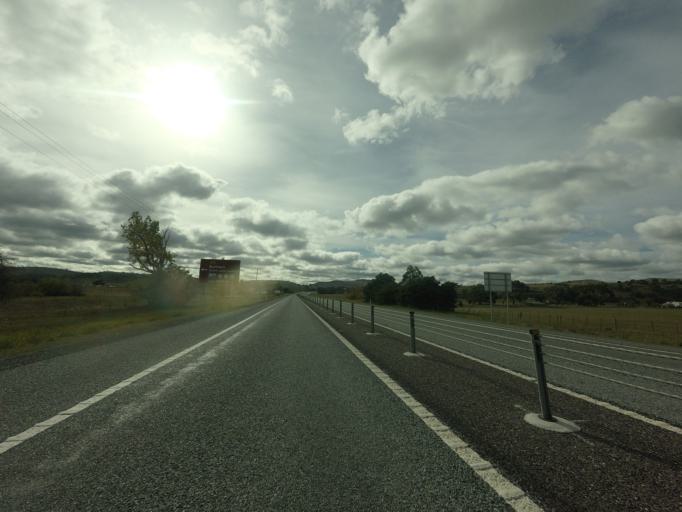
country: AU
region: Tasmania
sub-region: Brighton
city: Bridgewater
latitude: -42.4751
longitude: 147.1806
